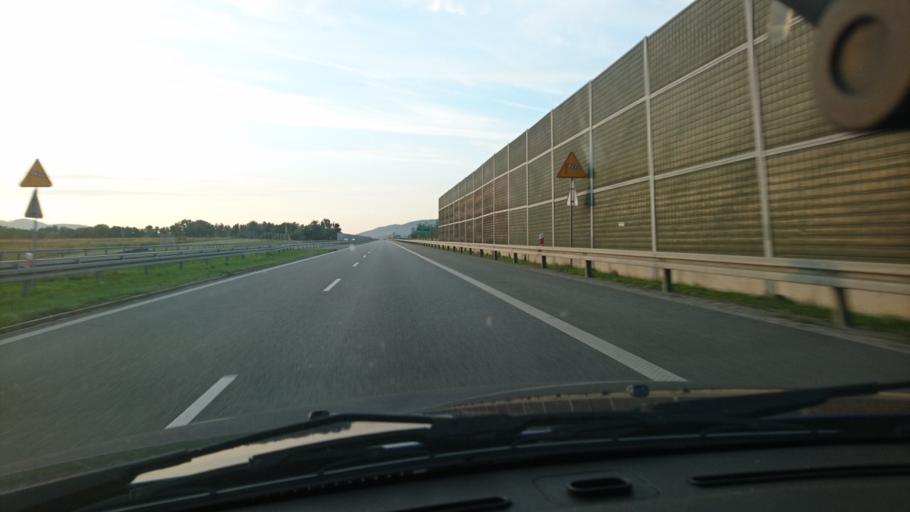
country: PL
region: Silesian Voivodeship
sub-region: Powiat zywiecki
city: Lodygowice
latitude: 49.7212
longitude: 19.1213
